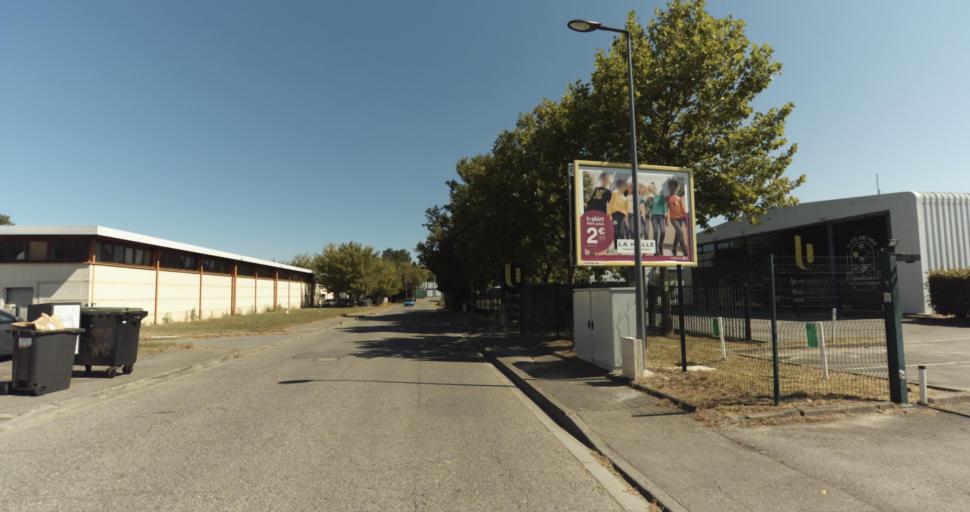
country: FR
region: Midi-Pyrenees
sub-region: Departement de la Haute-Garonne
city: L'Union
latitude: 43.6392
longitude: 1.4948
